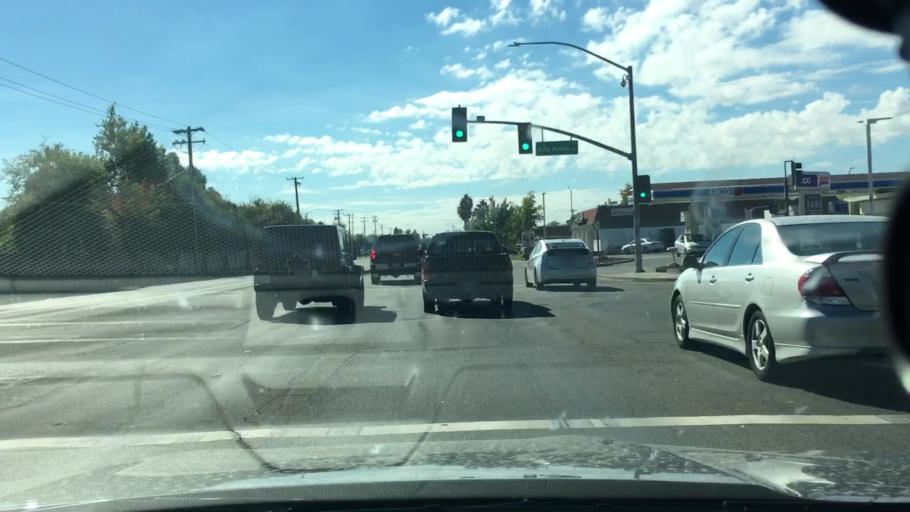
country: US
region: California
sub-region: Sacramento County
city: Arden-Arcade
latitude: 38.5991
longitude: -121.3831
